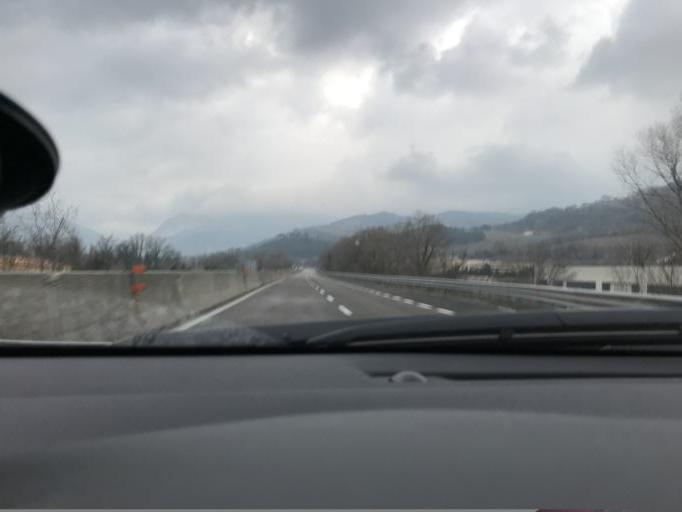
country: IT
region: The Marches
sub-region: Provincia di Ancona
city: Rosora
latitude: 43.4632
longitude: 13.0605
